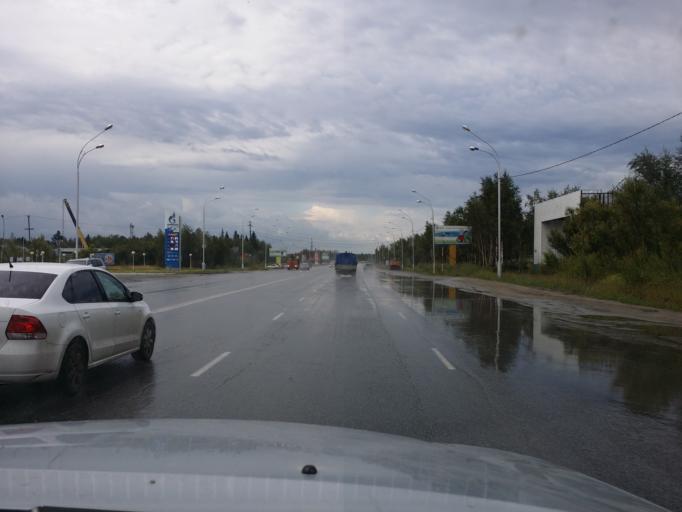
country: RU
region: Khanty-Mansiyskiy Avtonomnyy Okrug
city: Nizhnevartovsk
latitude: 60.9622
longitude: 76.5306
